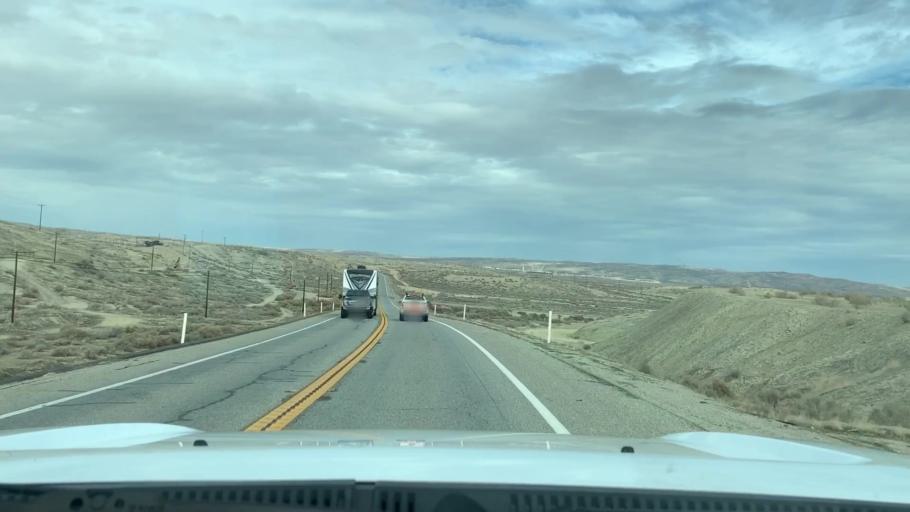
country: US
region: California
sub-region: Kern County
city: Maricopa
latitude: 35.0813
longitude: -119.4008
